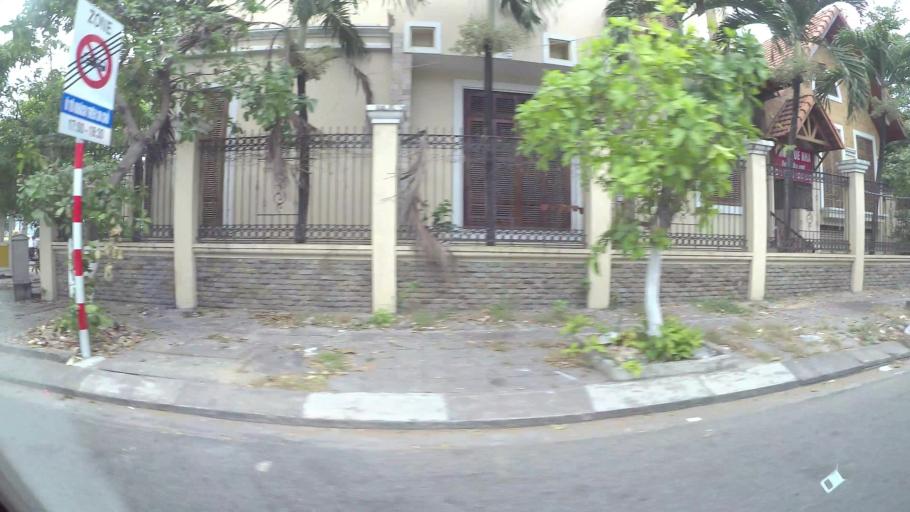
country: VN
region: Da Nang
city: Thanh Khe
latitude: 16.0721
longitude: 108.1919
